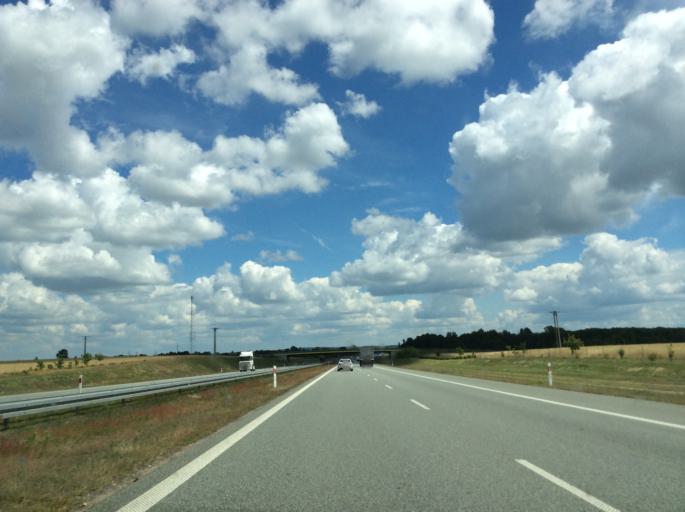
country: PL
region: Greater Poland Voivodeship
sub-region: Powiat koninski
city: Krzymow
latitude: 52.1414
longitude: 18.3739
